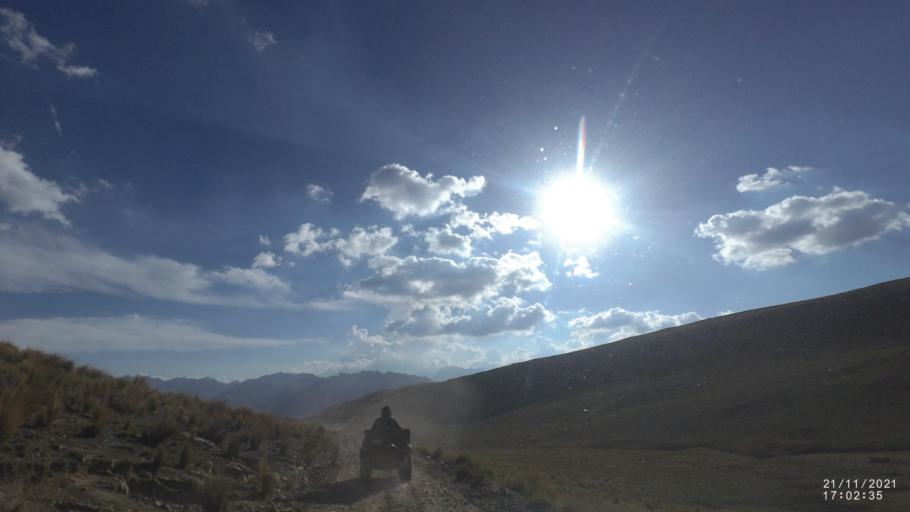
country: BO
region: Cochabamba
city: Cochabamba
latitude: -17.1169
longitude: -66.2550
